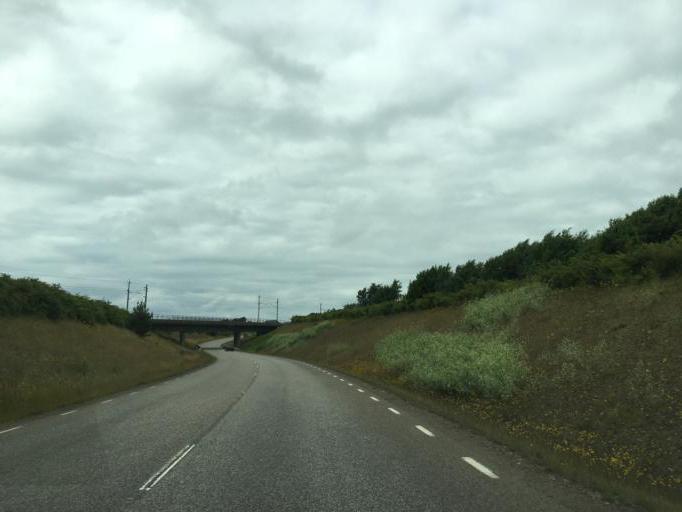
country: SE
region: Skane
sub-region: Bastads Kommun
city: Forslov
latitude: 56.3027
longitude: 12.8227
